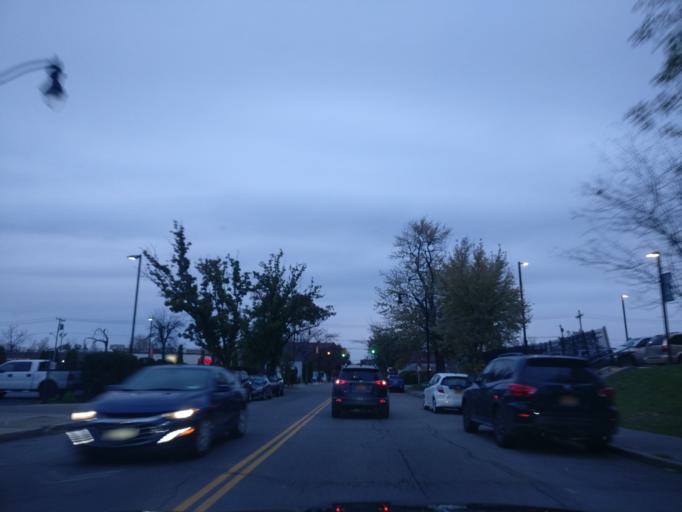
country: US
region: New York
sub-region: Erie County
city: Buffalo
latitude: 42.9042
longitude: -78.8909
